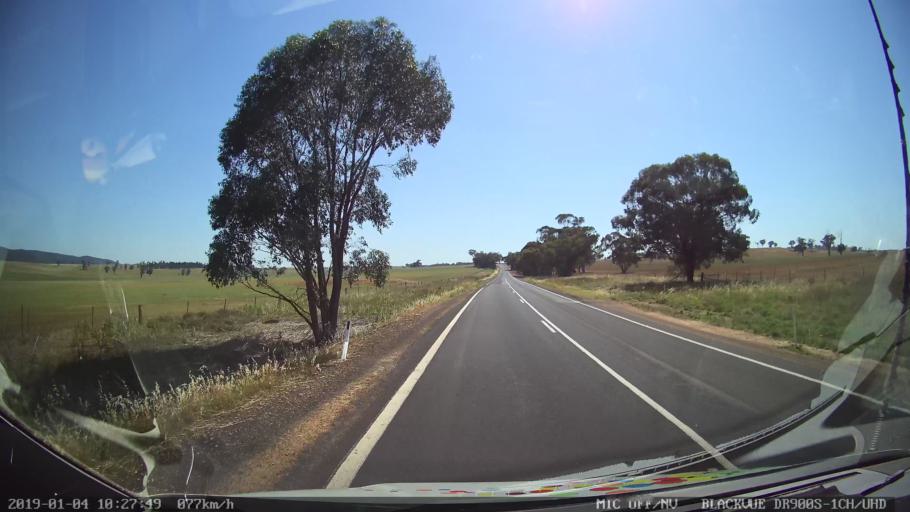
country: AU
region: New South Wales
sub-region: Cabonne
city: Canowindra
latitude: -33.3669
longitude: 148.6023
